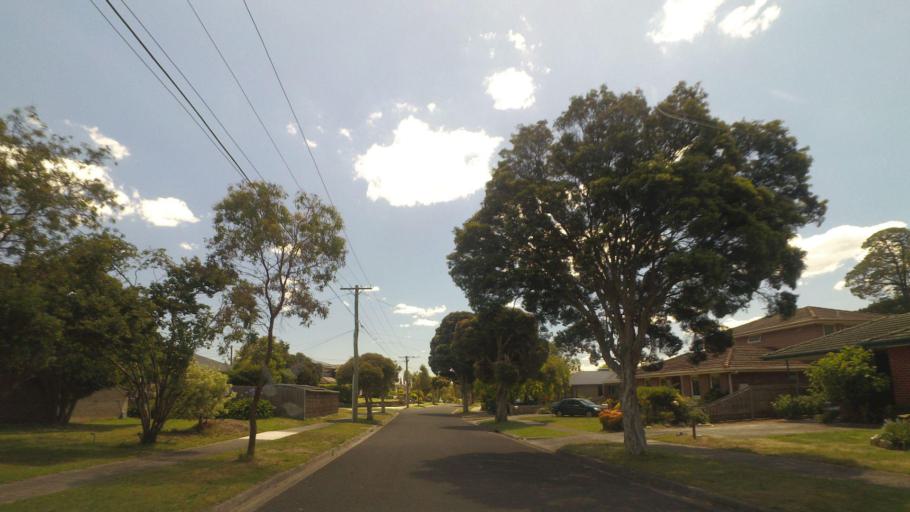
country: AU
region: Victoria
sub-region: Yarra Ranges
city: Kilsyth
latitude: -37.8037
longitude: 145.3283
